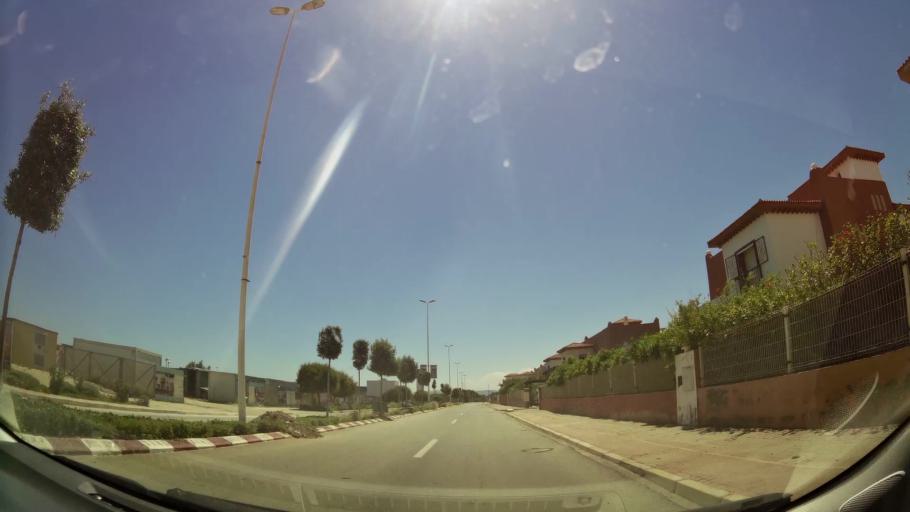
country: MA
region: Oriental
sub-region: Berkane-Taourirt
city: Madagh
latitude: 35.1059
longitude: -2.3019
